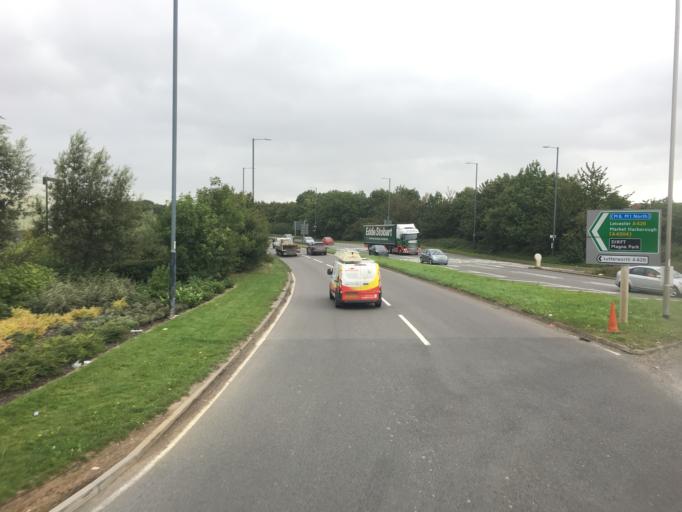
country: GB
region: England
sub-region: Warwickshire
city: Rugby
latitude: 52.4032
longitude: -1.2466
